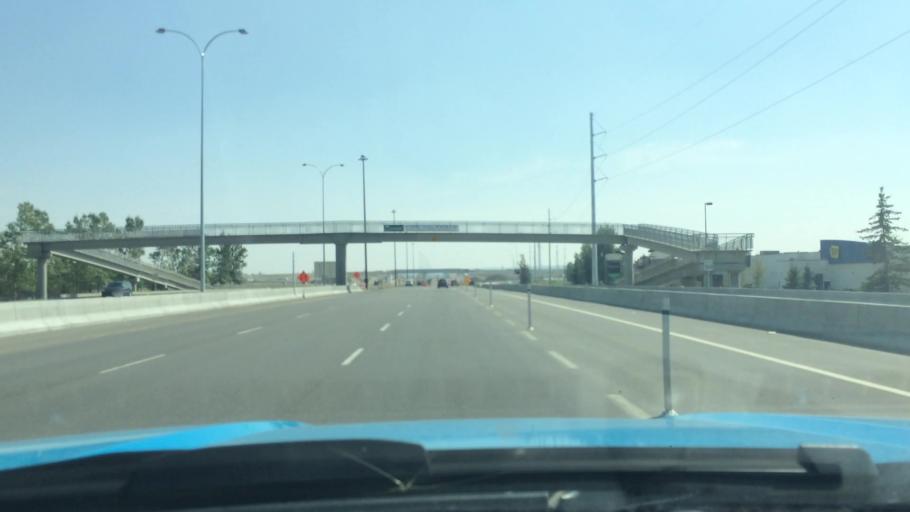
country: CA
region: Alberta
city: Calgary
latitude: 50.9014
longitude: -114.0601
